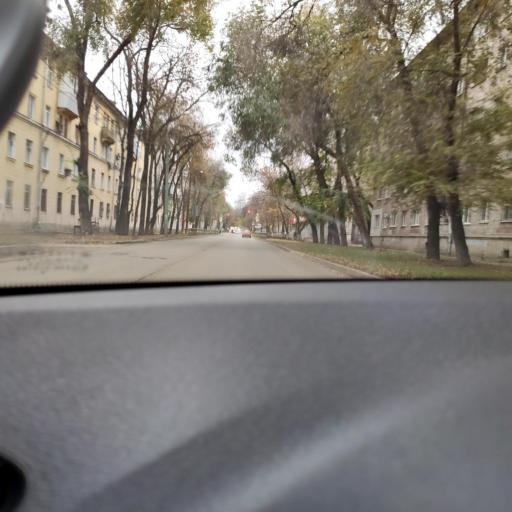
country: RU
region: Samara
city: Samara
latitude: 53.2143
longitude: 50.2422
